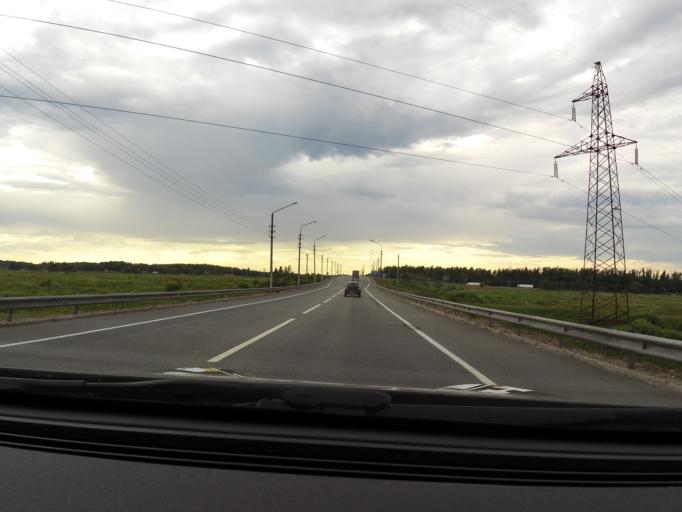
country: RU
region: Vladimir
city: Vorsha
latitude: 56.0778
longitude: 40.2069
